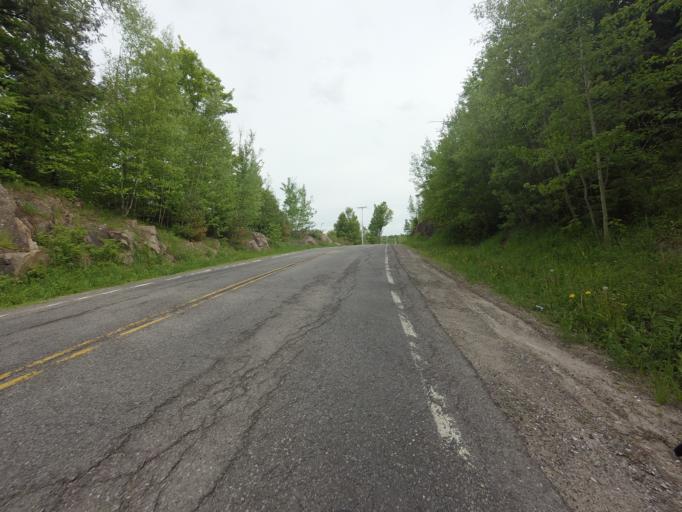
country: US
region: New York
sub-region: St. Lawrence County
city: Gouverneur
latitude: 44.3192
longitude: -75.2437
